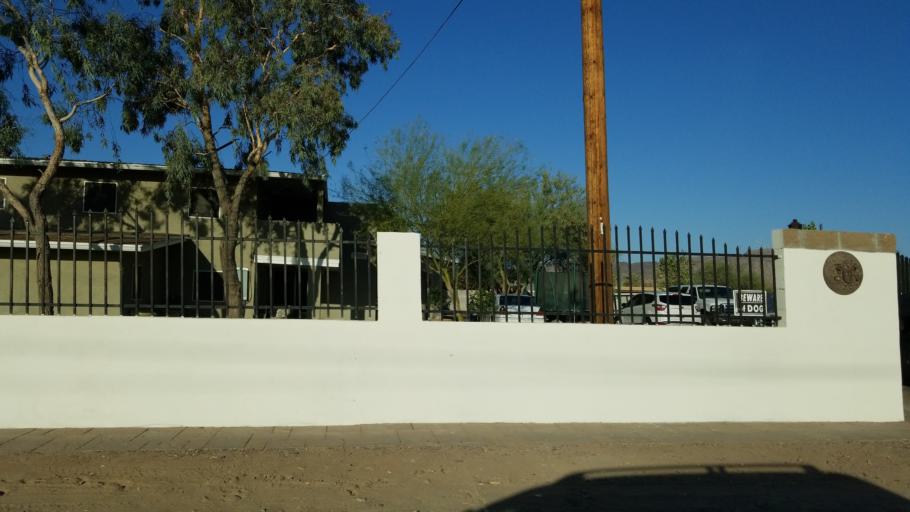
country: US
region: Arizona
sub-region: Maricopa County
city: Laveen
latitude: 33.3625
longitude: -112.1176
